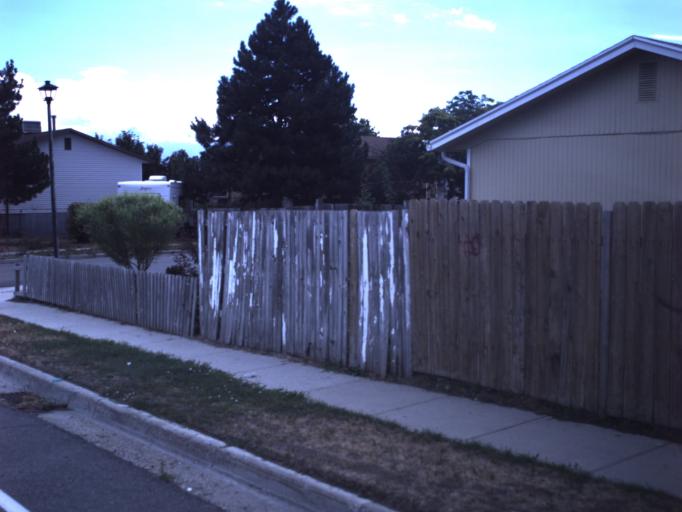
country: US
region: Utah
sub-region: Salt Lake County
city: Kearns
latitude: 40.6530
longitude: -112.0207
